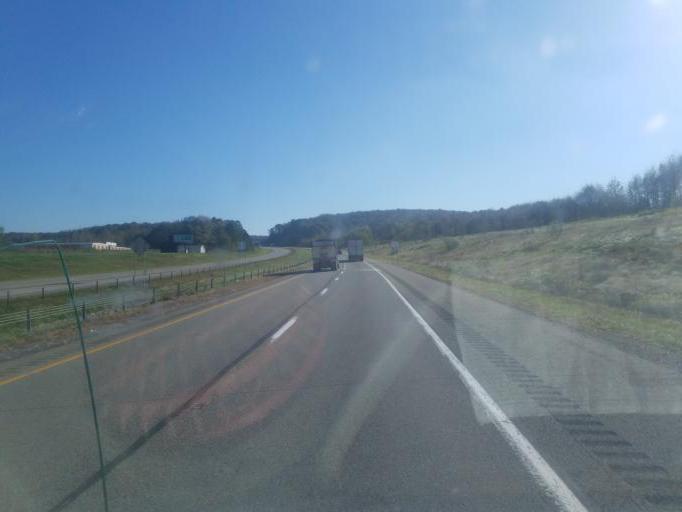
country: US
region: Pennsylvania
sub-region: Cambria County
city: Cresson
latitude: 40.4458
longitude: -78.5893
